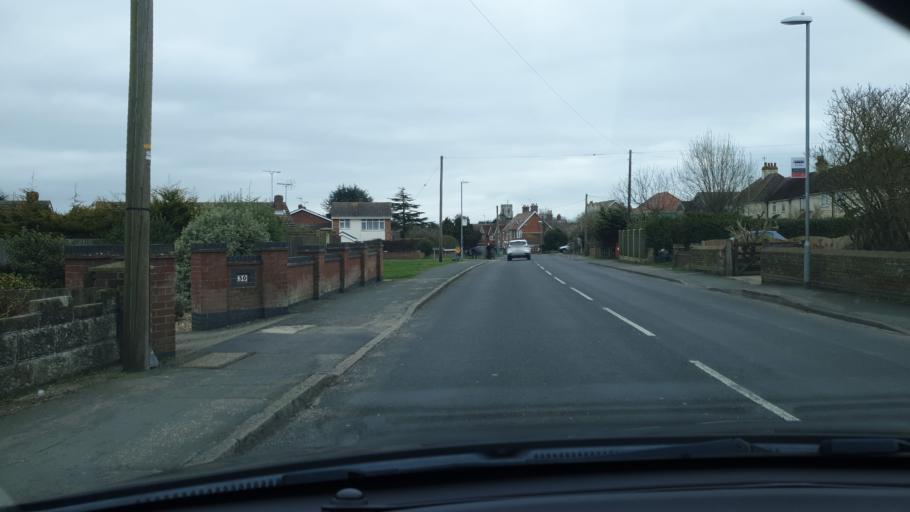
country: GB
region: England
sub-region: Essex
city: Walton-on-the-Naze
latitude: 51.8490
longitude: 1.2613
